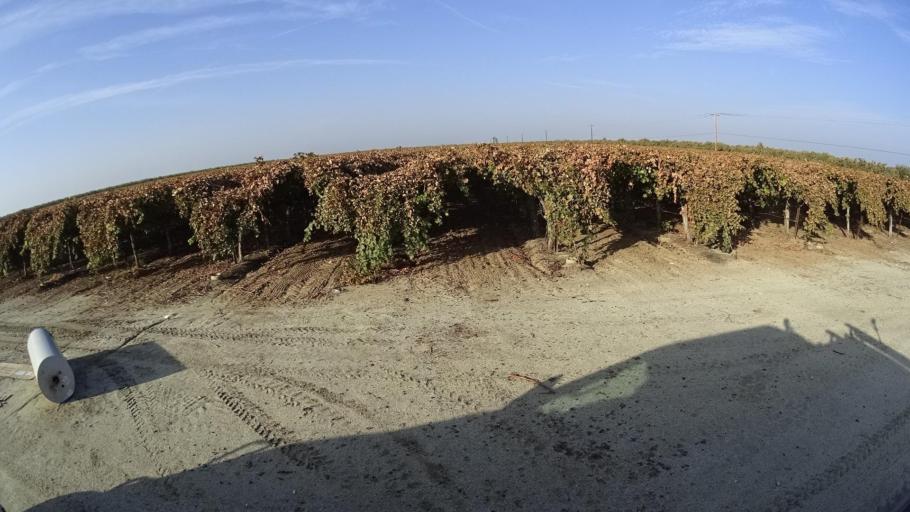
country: US
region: California
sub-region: Kern County
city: McFarland
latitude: 35.7173
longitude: -119.1873
